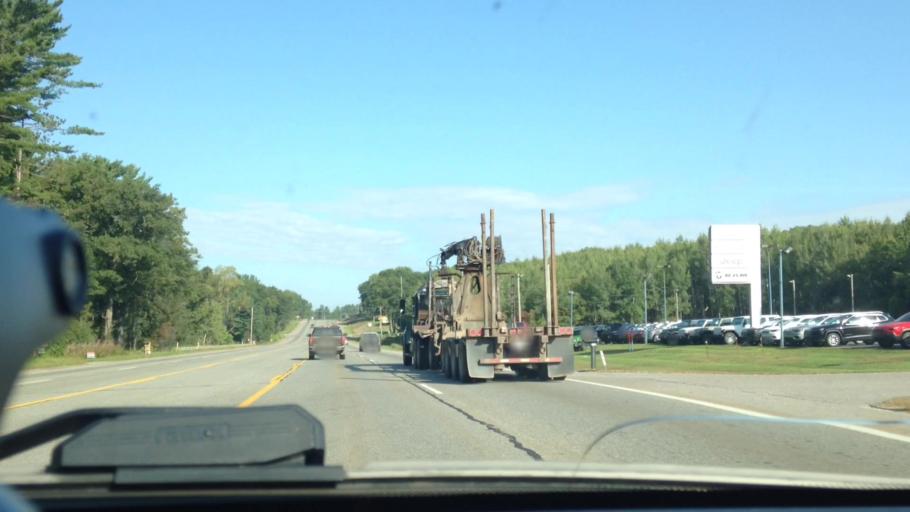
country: US
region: Michigan
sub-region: Dickinson County
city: Iron Mountain
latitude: 45.8518
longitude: -88.0537
